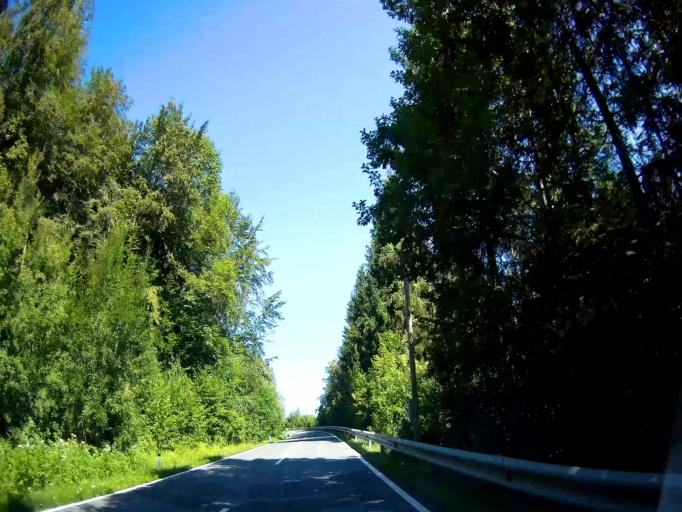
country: AT
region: Carinthia
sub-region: Politischer Bezirk Volkermarkt
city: Gallizien
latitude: 46.5538
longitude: 14.4908
